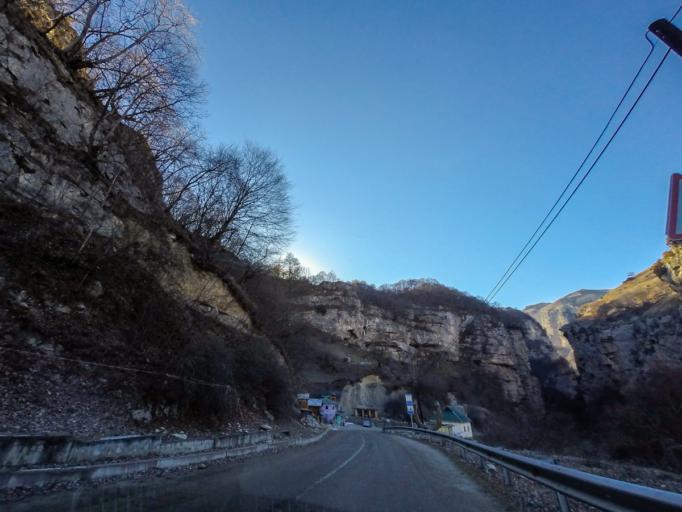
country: RU
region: Kabardino-Balkariya
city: Zhankhoteko
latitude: 43.4242
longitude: 43.2325
